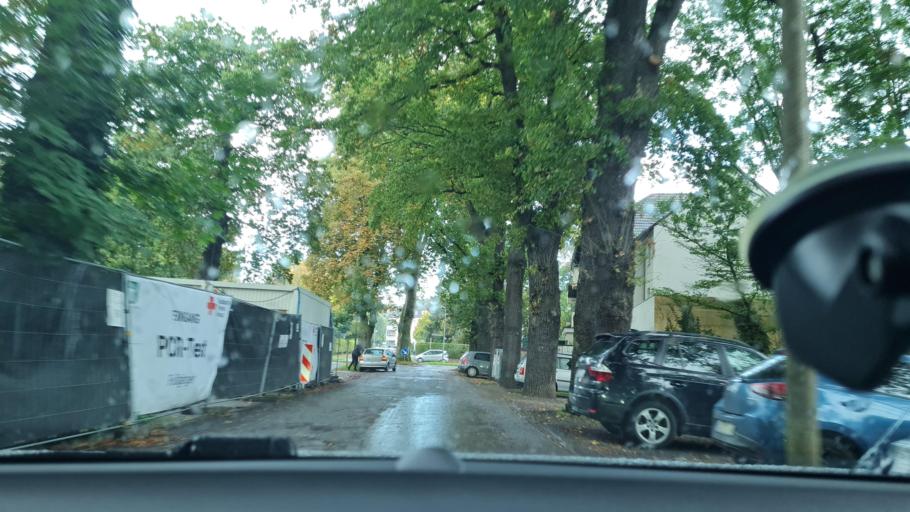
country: DE
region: North Rhine-Westphalia
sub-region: Regierungsbezirk Dusseldorf
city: Dinslaken
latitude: 51.5572
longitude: 6.7356
